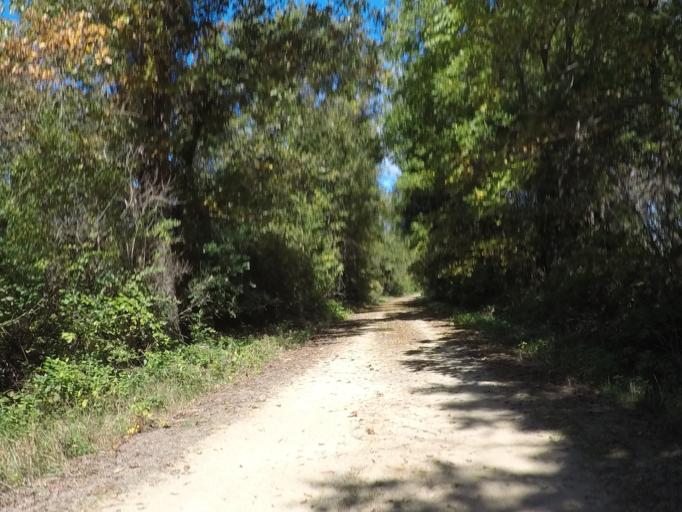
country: US
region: Wisconsin
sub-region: Richland County
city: Richland Center
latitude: 43.2244
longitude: -90.2972
